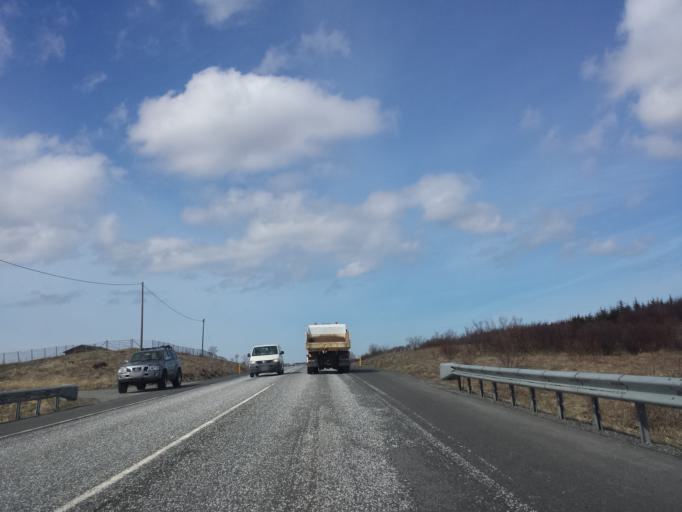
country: IS
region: Capital Region
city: Mosfellsbaer
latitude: 64.0983
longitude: -21.7459
